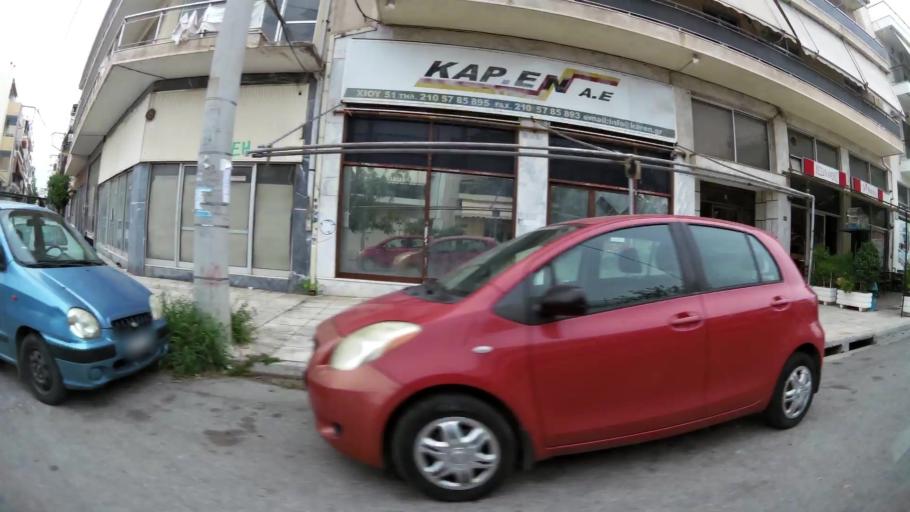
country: GR
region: Attica
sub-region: Nomarchia Athinas
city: Peristeri
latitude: 38.0219
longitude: 23.6983
